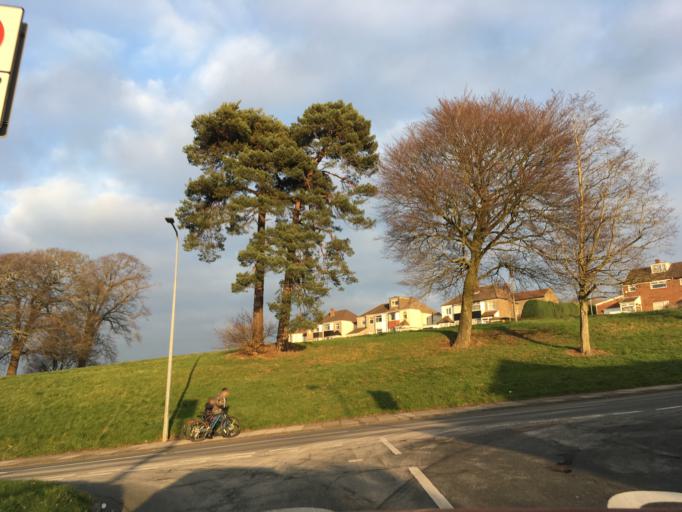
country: GB
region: Wales
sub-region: Cardiff
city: Cardiff
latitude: 51.5171
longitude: -3.1319
